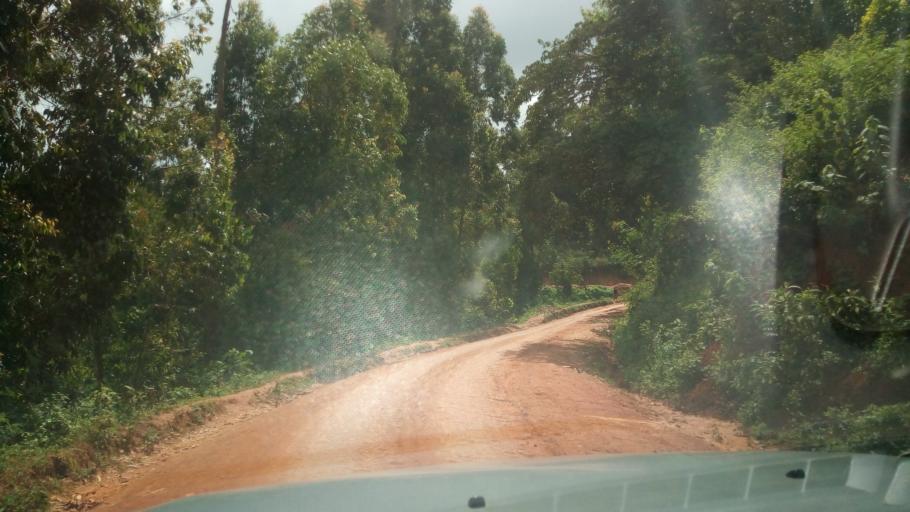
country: KE
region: Makueni
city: Wote
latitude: -1.6708
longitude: 37.4500
